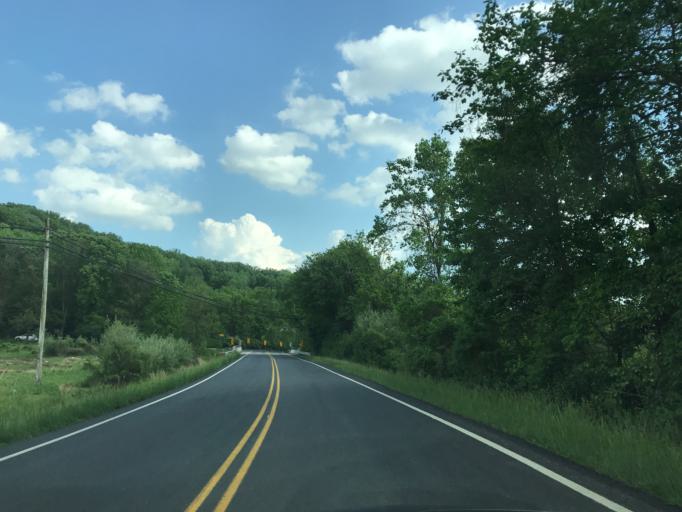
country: US
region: Maryland
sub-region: Harford County
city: Bel Air North
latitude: 39.5460
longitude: -76.3930
